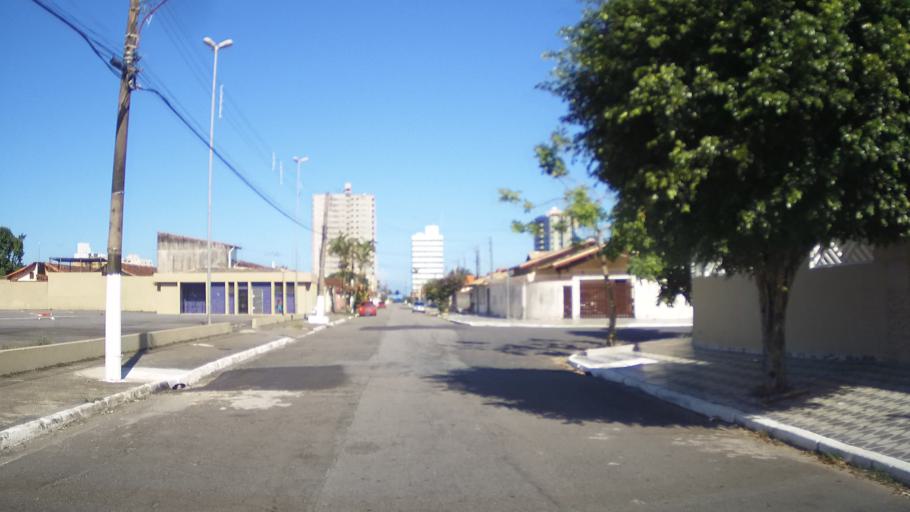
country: BR
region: Sao Paulo
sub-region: Mongagua
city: Mongagua
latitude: -24.0618
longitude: -46.5583
